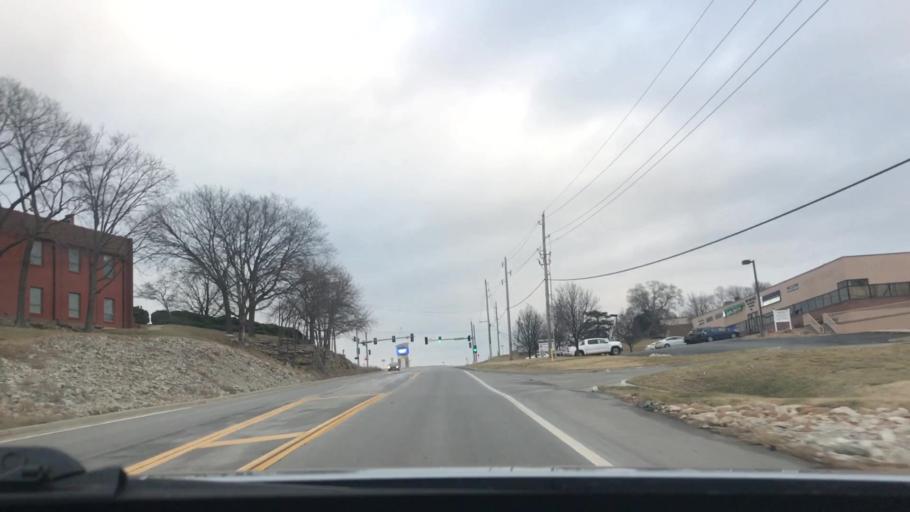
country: US
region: Missouri
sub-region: Platte County
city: Platte City
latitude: 39.3669
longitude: -94.7766
